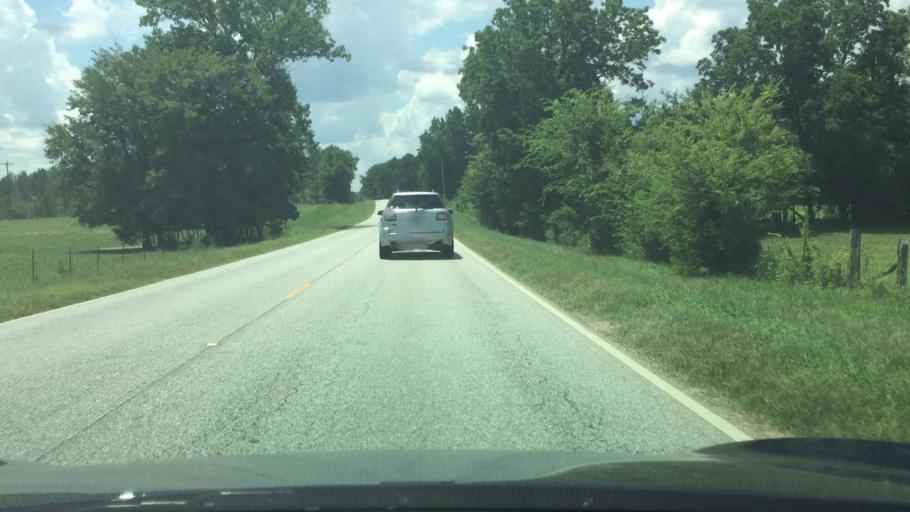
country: US
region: Alabama
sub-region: Montgomery County
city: Pike Road
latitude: 32.2344
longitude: -86.0931
